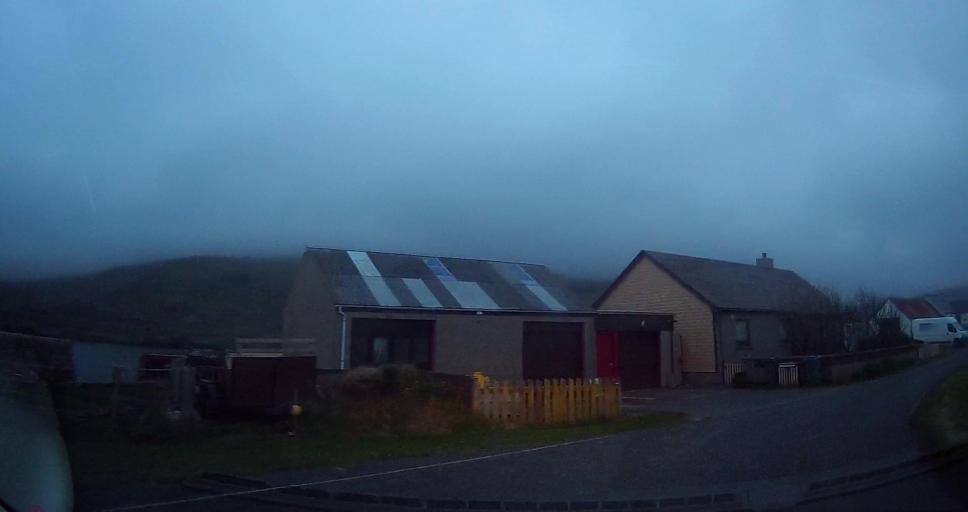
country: GB
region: Scotland
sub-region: Shetland Islands
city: Sandwick
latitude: 60.0339
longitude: -1.2257
